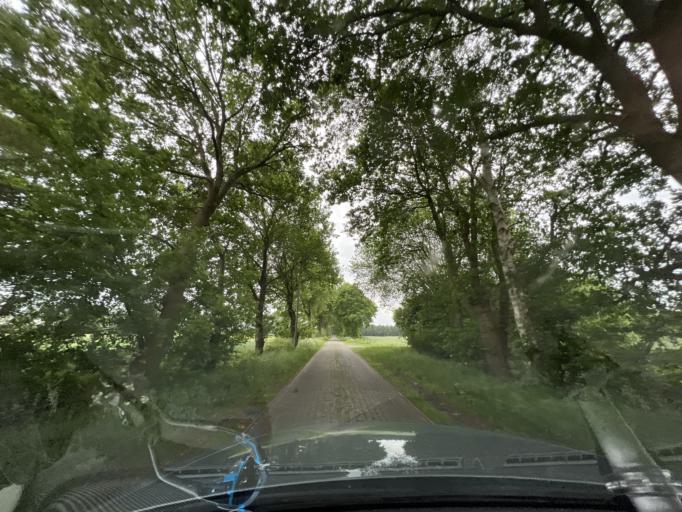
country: DE
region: Lower Saxony
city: Hatten
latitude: 53.0416
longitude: 8.3153
